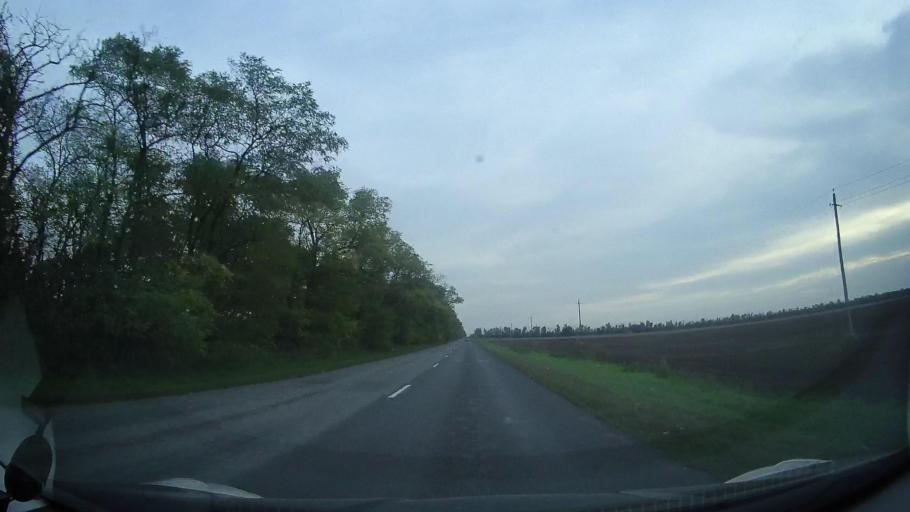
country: RU
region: Rostov
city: Ol'ginskaya
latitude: 47.1050
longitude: 39.9775
